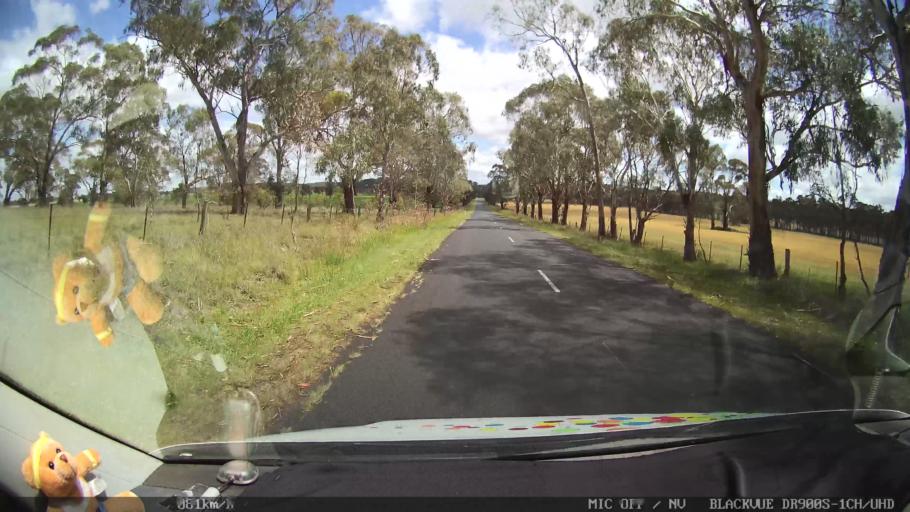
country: AU
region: New South Wales
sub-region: Glen Innes Severn
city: Glen Innes
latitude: -29.6073
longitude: 151.6670
